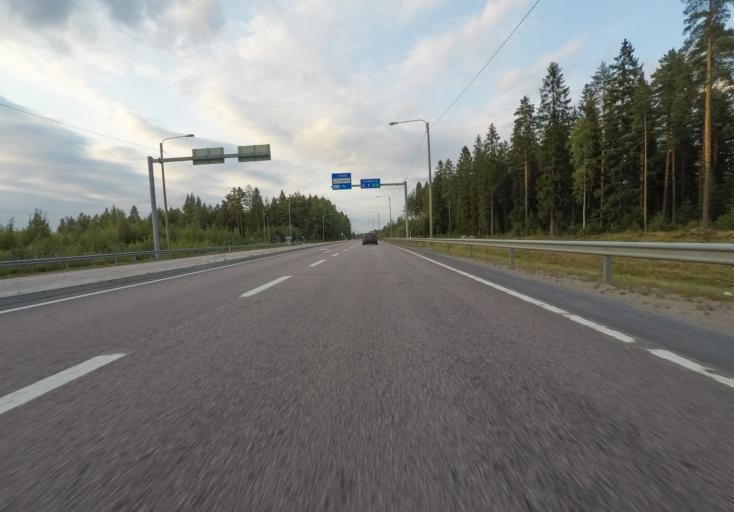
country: FI
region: Paijanne Tavastia
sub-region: Lahti
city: Hartola
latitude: 61.5798
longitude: 26.0077
